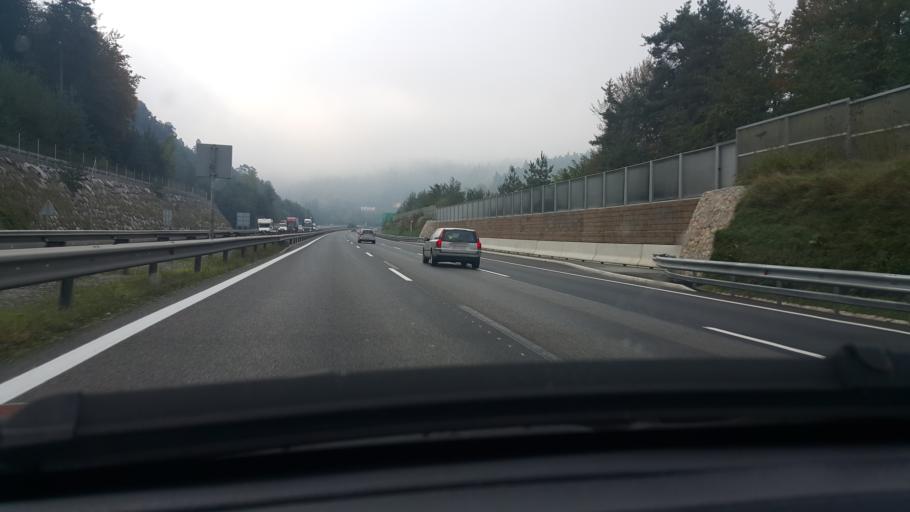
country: SI
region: Skofljica
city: Lavrica
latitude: 46.0279
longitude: 14.5679
